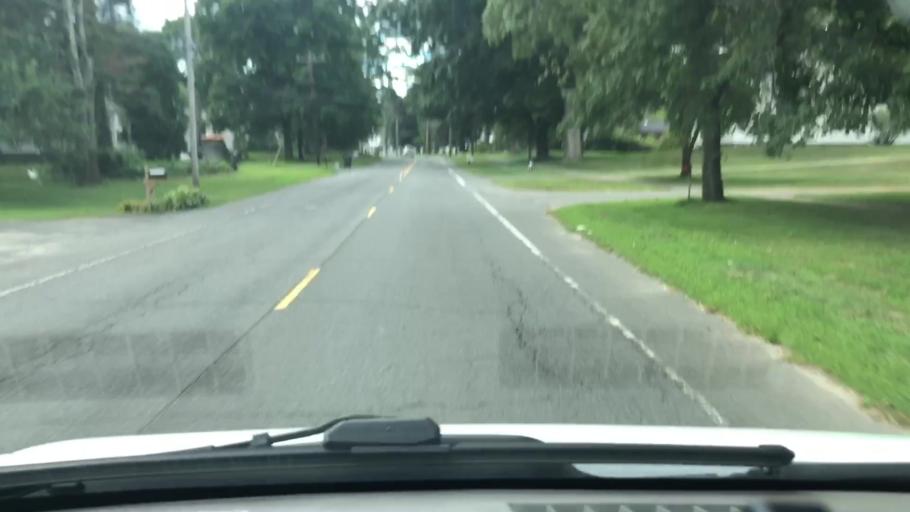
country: US
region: Massachusetts
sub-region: Hampshire County
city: Hatfield
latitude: 42.3657
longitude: -72.6091
